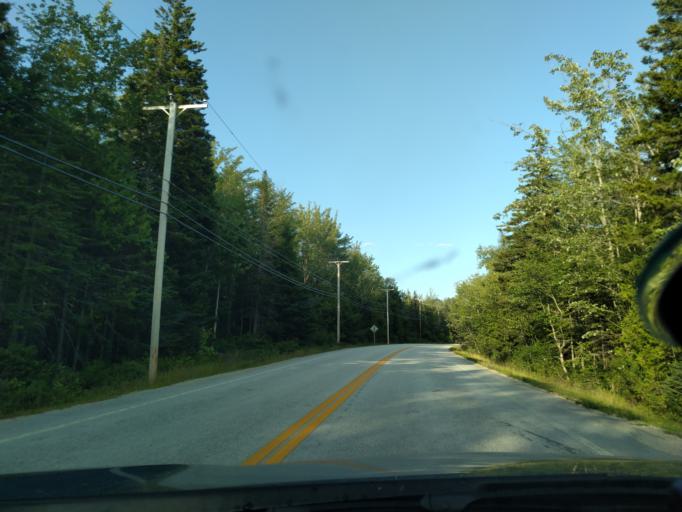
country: US
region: Maine
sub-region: Hancock County
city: Gouldsboro
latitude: 44.3938
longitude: -68.0679
